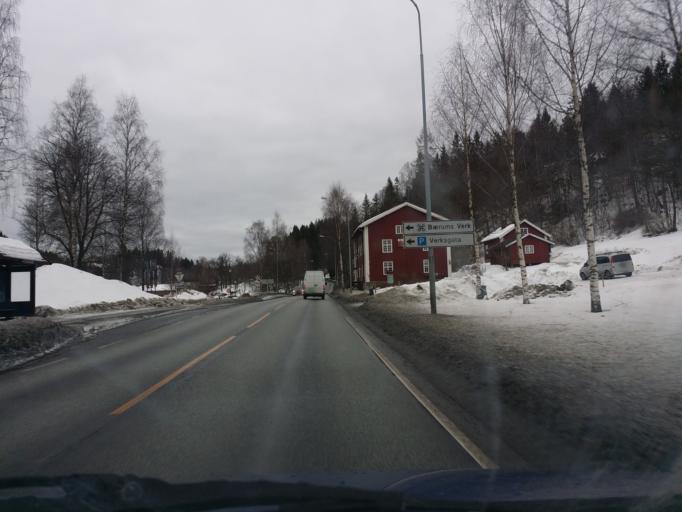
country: NO
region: Akershus
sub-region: Baerum
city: Sandvika
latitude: 59.9371
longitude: 10.5013
